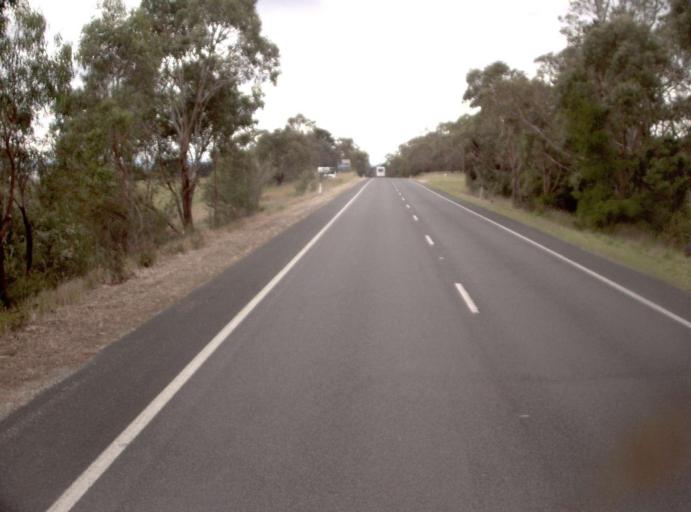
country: AU
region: Victoria
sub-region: Wellington
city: Sale
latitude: -38.1826
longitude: 147.0826
